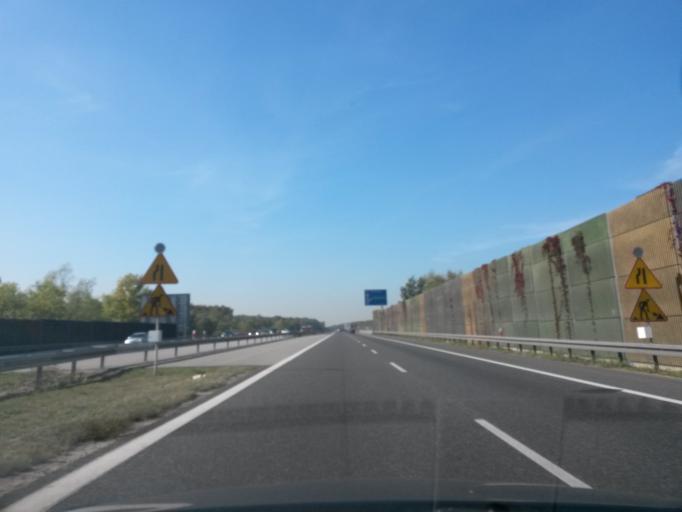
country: PL
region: Silesian Voivodeship
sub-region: Myslowice
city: Myslowice
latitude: 50.2115
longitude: 19.1506
